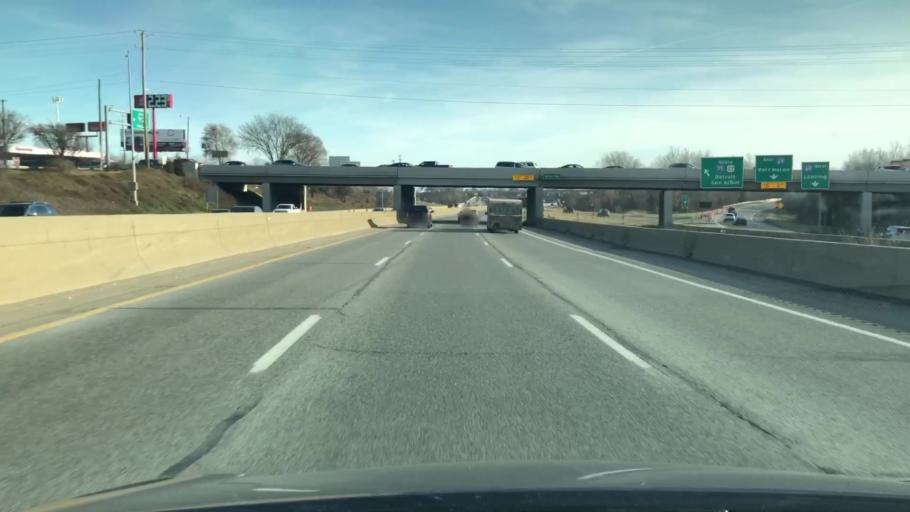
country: US
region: Michigan
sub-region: Genesee County
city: Flint
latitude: 42.9903
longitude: -83.7397
